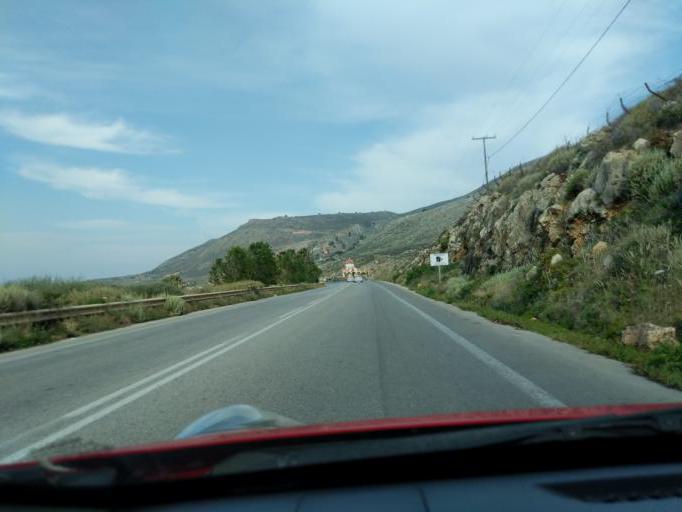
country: GR
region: Crete
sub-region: Nomos Rethymnis
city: Atsipopoulon
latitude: 35.3506
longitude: 24.3546
